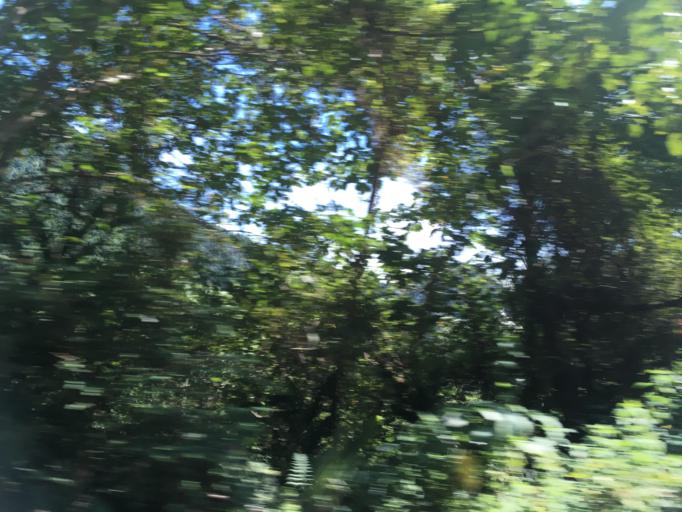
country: TW
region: Taiwan
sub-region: Yilan
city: Yilan
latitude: 24.4391
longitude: 121.7628
